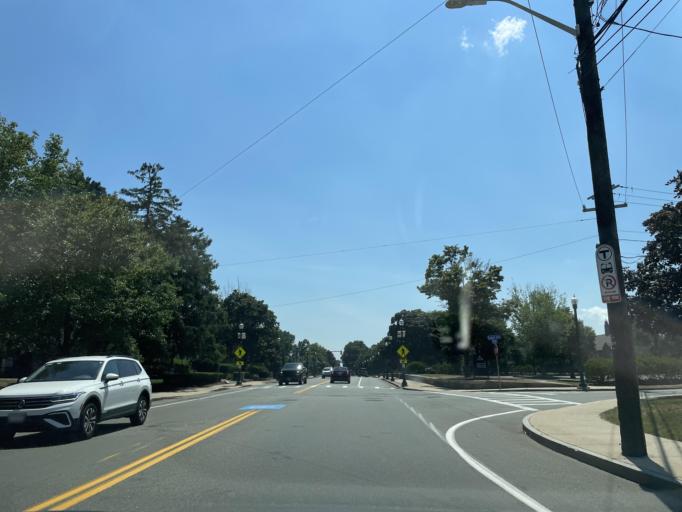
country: US
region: Massachusetts
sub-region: Norfolk County
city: Braintree
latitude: 42.2094
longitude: -71.0033
